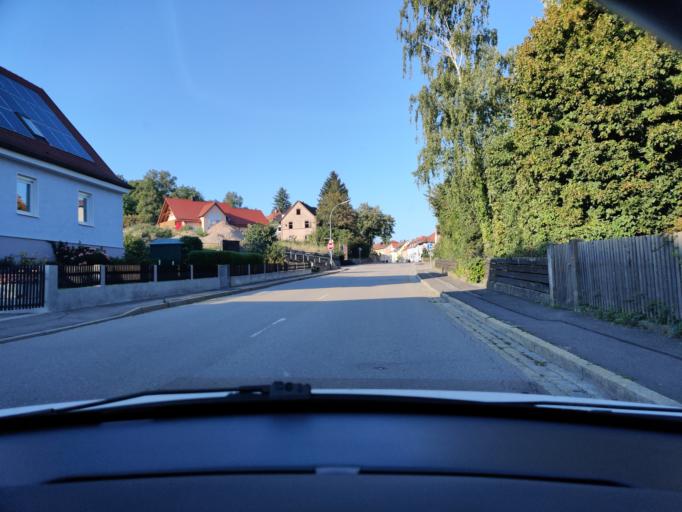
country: DE
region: Bavaria
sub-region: Upper Palatinate
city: Nabburg
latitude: 49.4487
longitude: 12.1765
